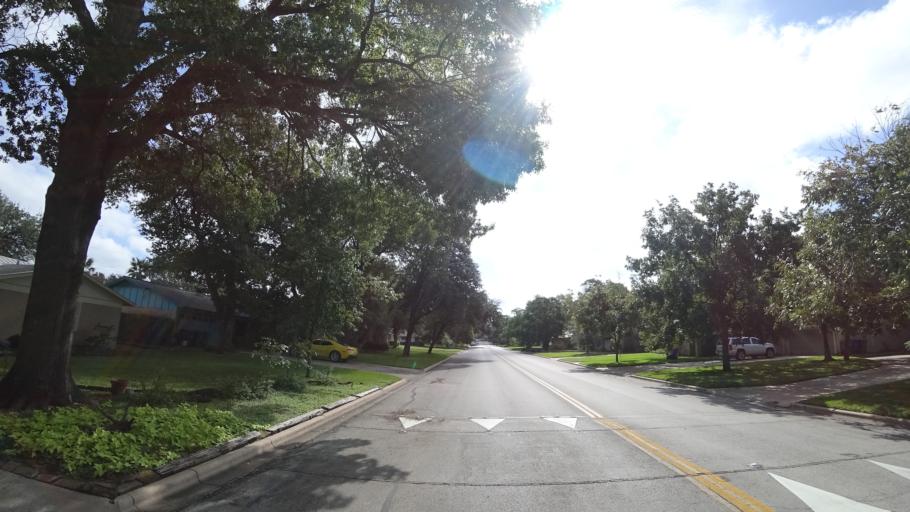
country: US
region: Texas
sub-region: Travis County
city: West Lake Hills
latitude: 30.3504
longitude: -97.7399
